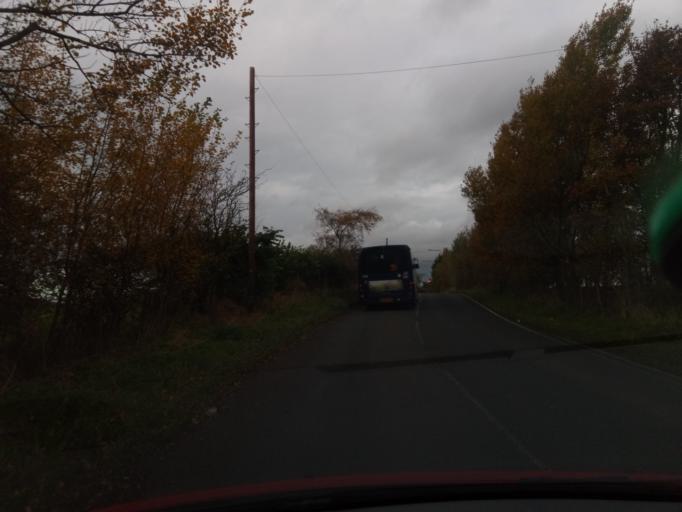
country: GB
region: Scotland
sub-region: West Lothian
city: Blackburn
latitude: 55.8507
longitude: -3.6157
